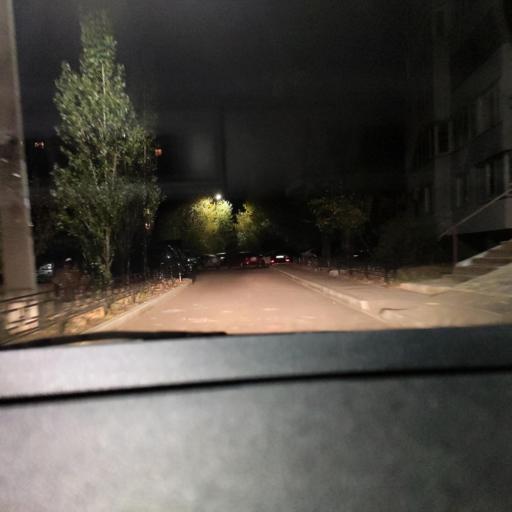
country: RU
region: Voronezj
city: Podgornoye
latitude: 51.7054
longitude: 39.1415
